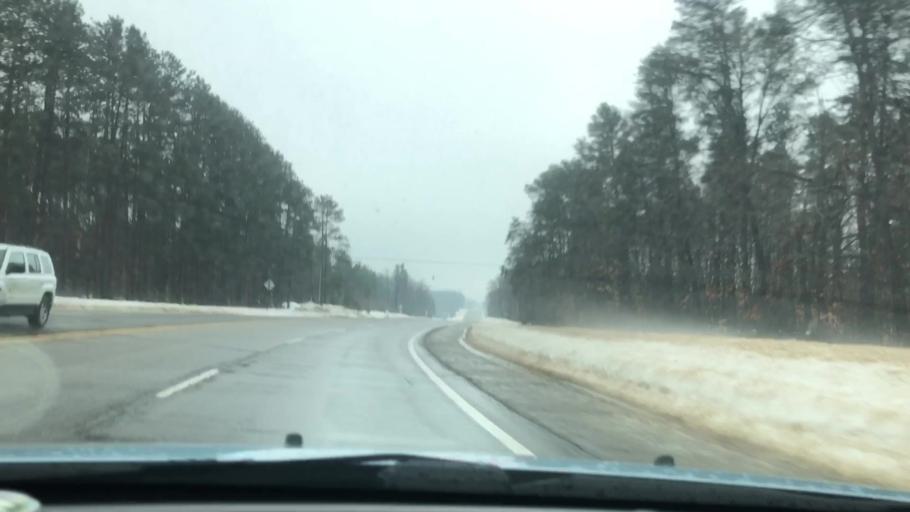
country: US
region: Michigan
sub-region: Otsego County
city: Gaylord
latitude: 45.0588
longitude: -84.7760
